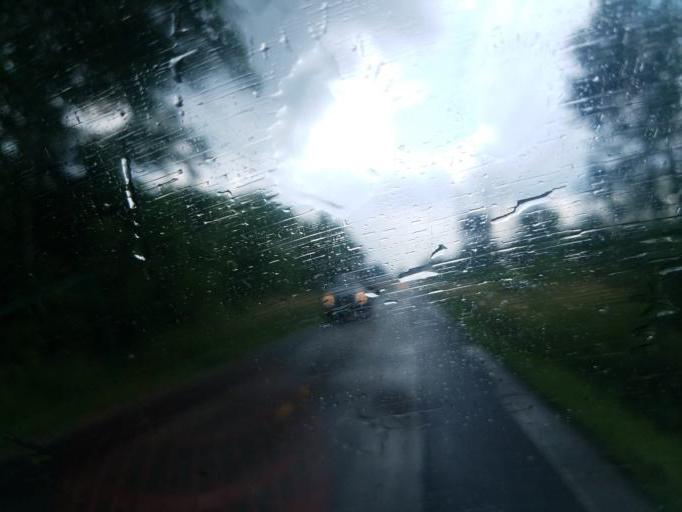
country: US
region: Ohio
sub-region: Columbiana County
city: Leetonia
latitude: 40.9437
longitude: -80.7487
